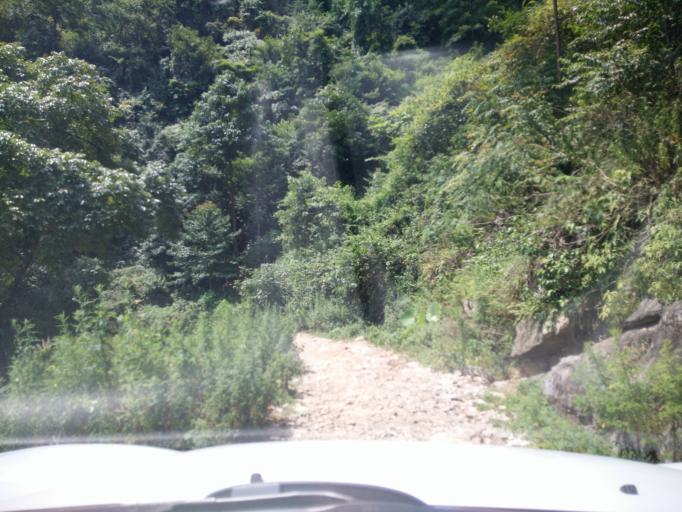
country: CN
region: Guangxi Zhuangzu Zizhiqu
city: Xinzhou
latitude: 25.0140
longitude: 105.7034
